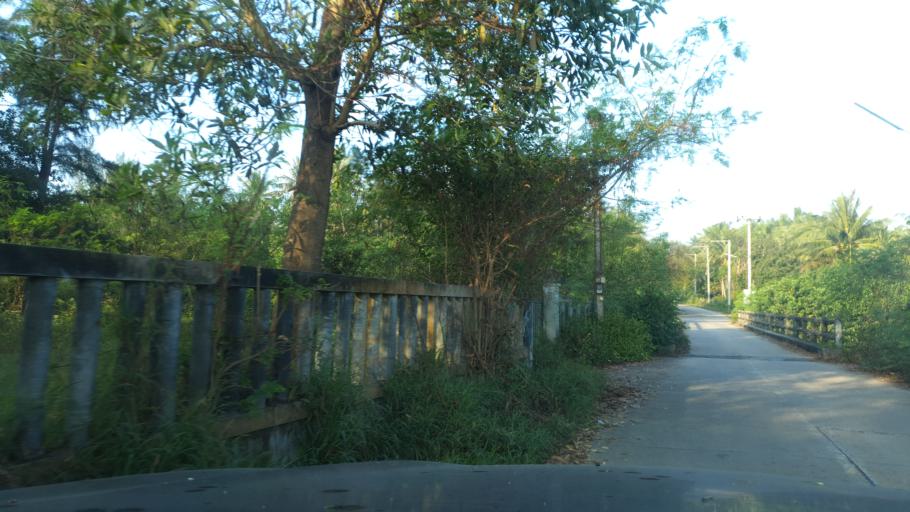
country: TH
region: Prachuap Khiri Khan
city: Bang Saphan
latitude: 11.3049
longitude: 99.5511
